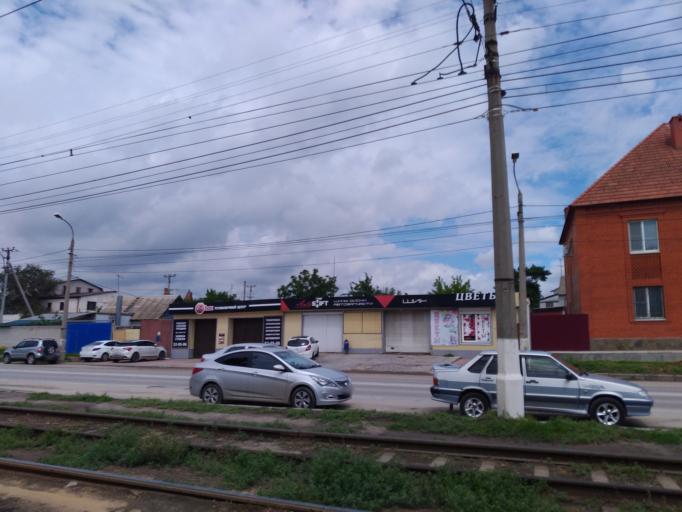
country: RU
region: Volgograd
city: Volgograd
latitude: 48.7157
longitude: 44.4893
